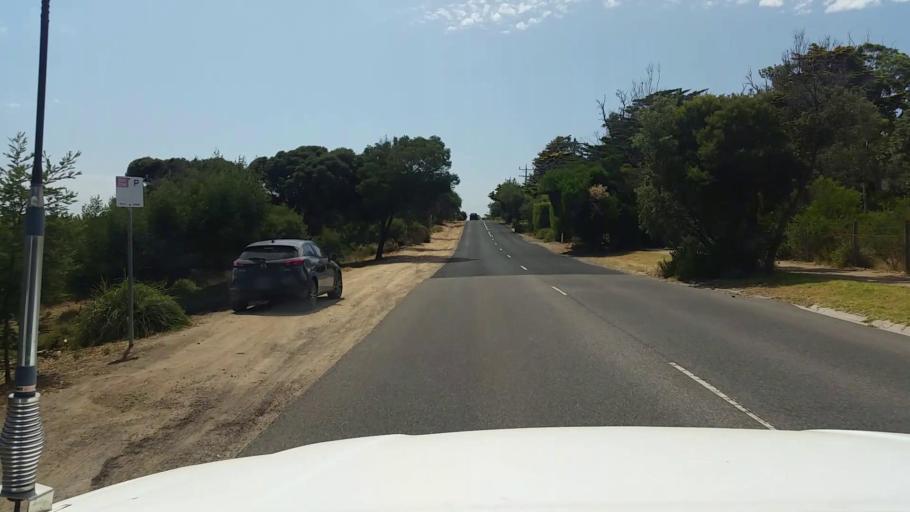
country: AU
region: Victoria
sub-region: Mornington Peninsula
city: Mount Martha
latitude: -38.2599
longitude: 145.0208
